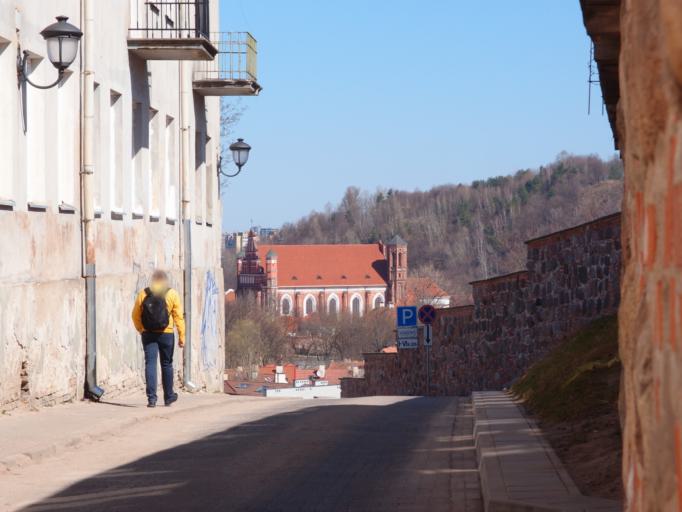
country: LT
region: Vilnius County
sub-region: Vilnius
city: Vilnius
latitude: 54.6773
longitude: 25.2923
